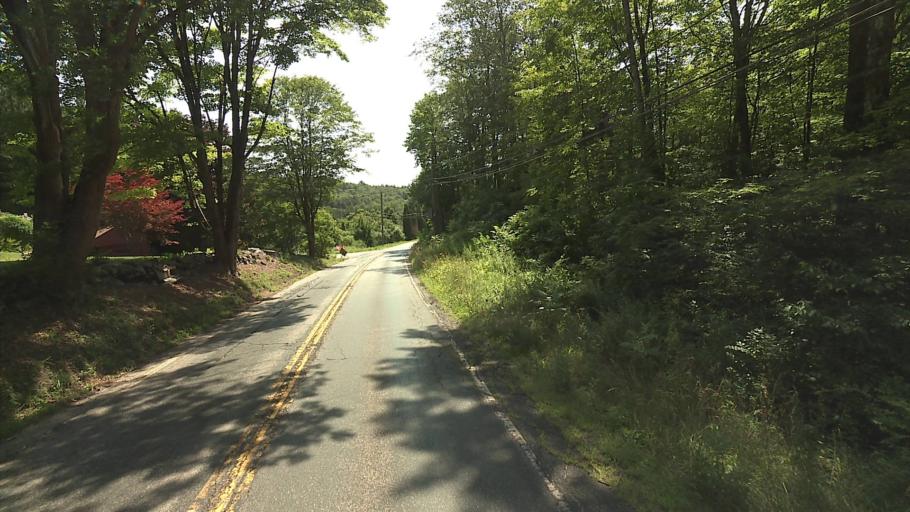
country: US
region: Connecticut
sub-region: Litchfield County
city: Winchester Center
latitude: 41.9165
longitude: -73.1907
